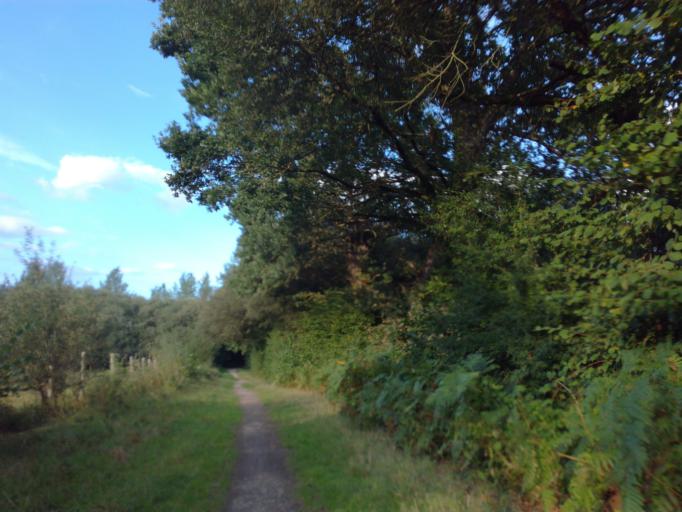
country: FR
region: Brittany
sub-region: Departement d'Ille-et-Vilaine
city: Fouillard
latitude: 48.1408
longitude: -1.5869
